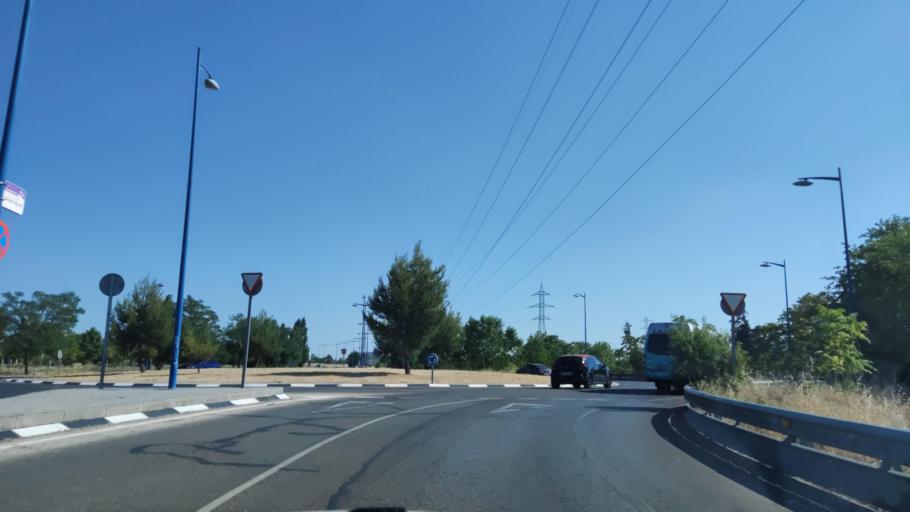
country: ES
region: Madrid
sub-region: Provincia de Madrid
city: Leganes
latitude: 40.3410
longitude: -3.7876
